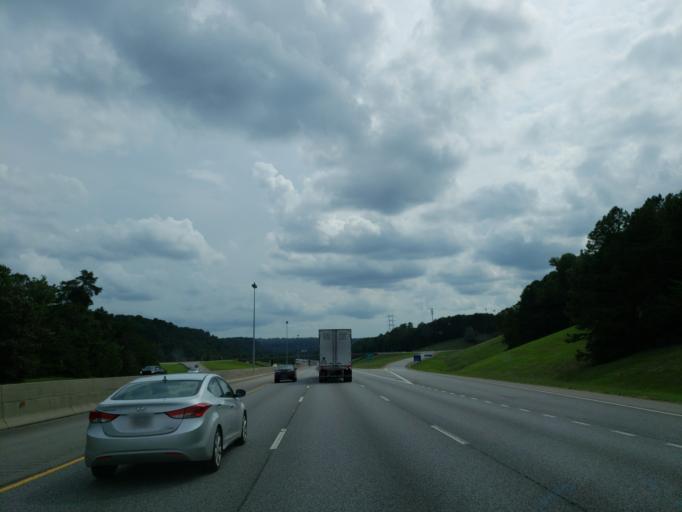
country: US
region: Alabama
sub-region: Jefferson County
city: Cahaba Heights
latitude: 33.4952
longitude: -86.7042
